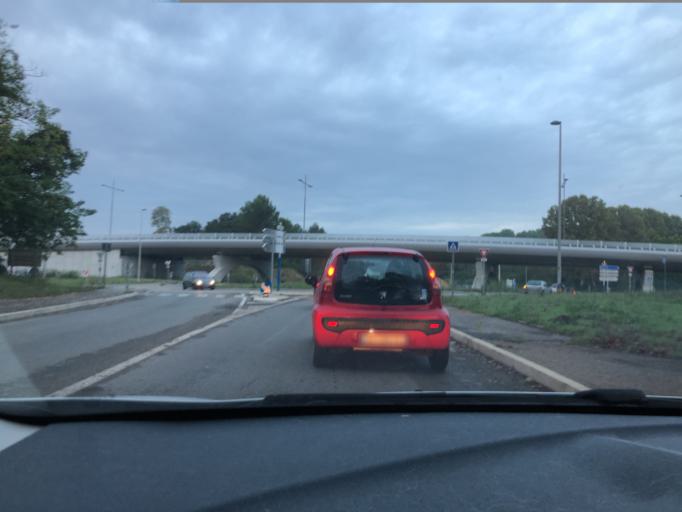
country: FR
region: Languedoc-Roussillon
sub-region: Departement de l'Herault
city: Montferrier-sur-Lez
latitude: 43.6518
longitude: 3.8658
